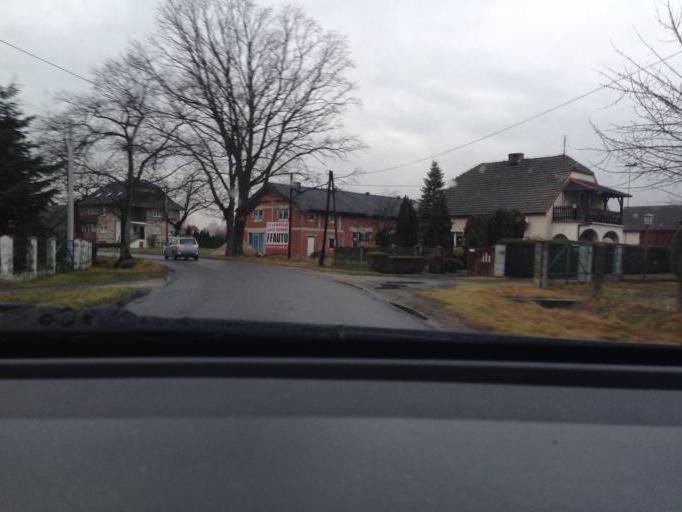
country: PL
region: Opole Voivodeship
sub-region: Powiat opolski
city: Chrzastowice
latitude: 50.7252
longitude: 18.0759
